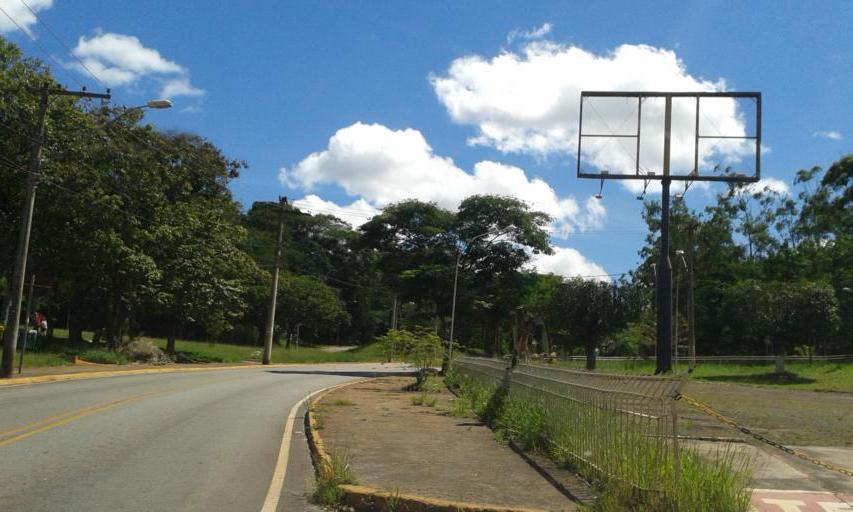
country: BR
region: Minas Gerais
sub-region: Itabira
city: Itabira
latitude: -19.6347
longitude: -43.2373
